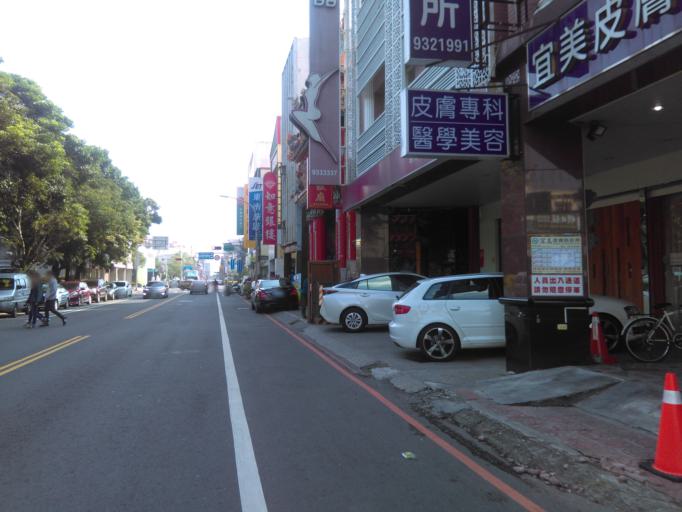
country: TW
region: Taiwan
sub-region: Yilan
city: Yilan
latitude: 24.7536
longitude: 121.7525
